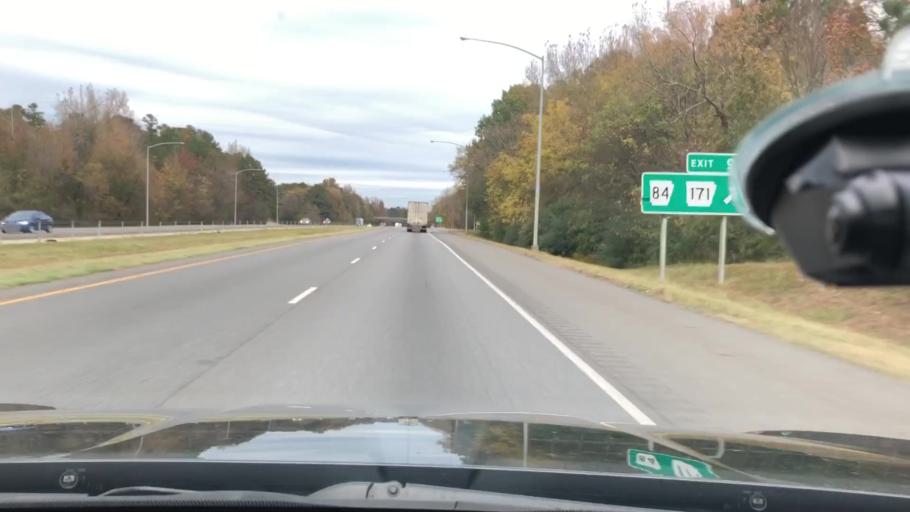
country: US
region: Arkansas
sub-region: Hot Spring County
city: Malvern
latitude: 34.3816
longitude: -92.8495
